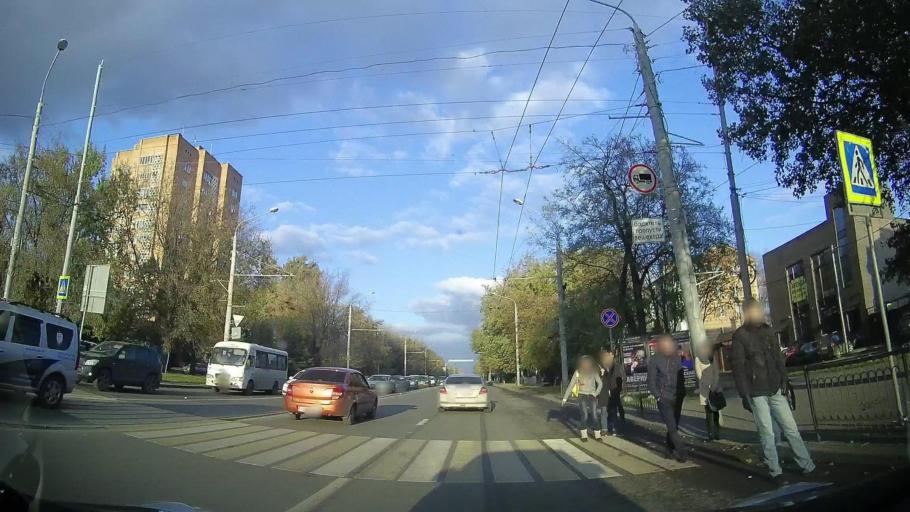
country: RU
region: Rostov
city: Imeni Chkalova
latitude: 47.2429
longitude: 39.7662
